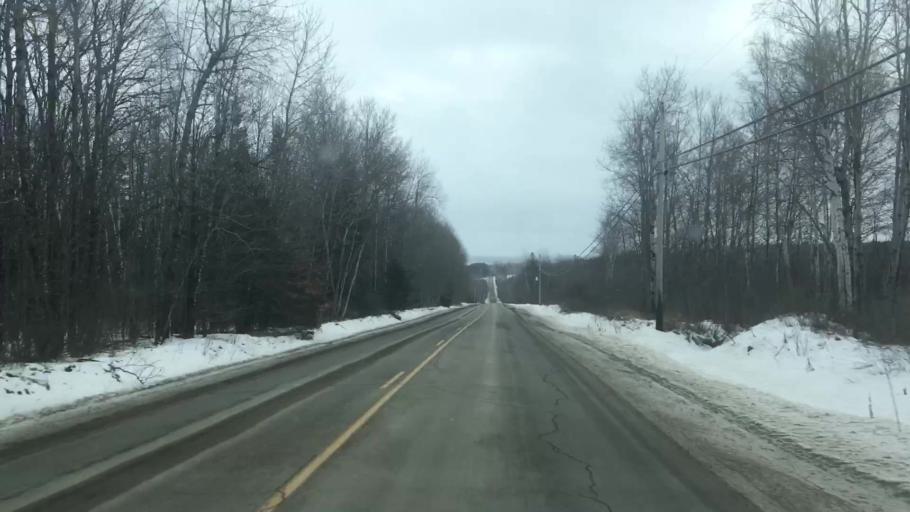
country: US
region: Maine
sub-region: Washington County
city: East Machias
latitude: 44.9740
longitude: -67.4499
